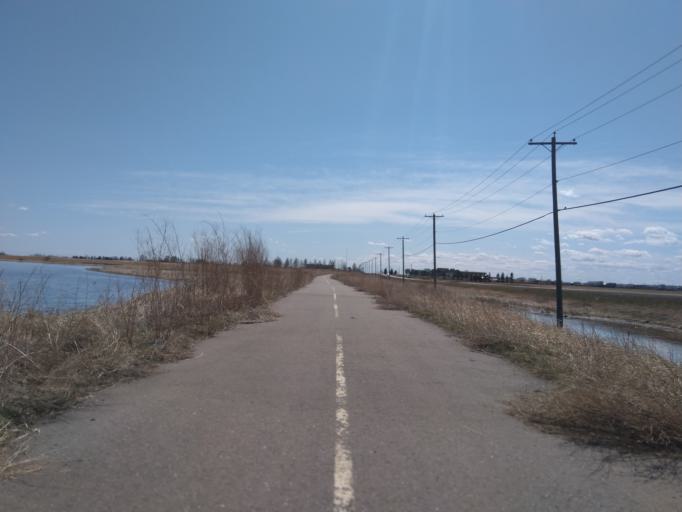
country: CA
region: Alberta
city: Chestermere
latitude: 50.9612
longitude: -113.9114
